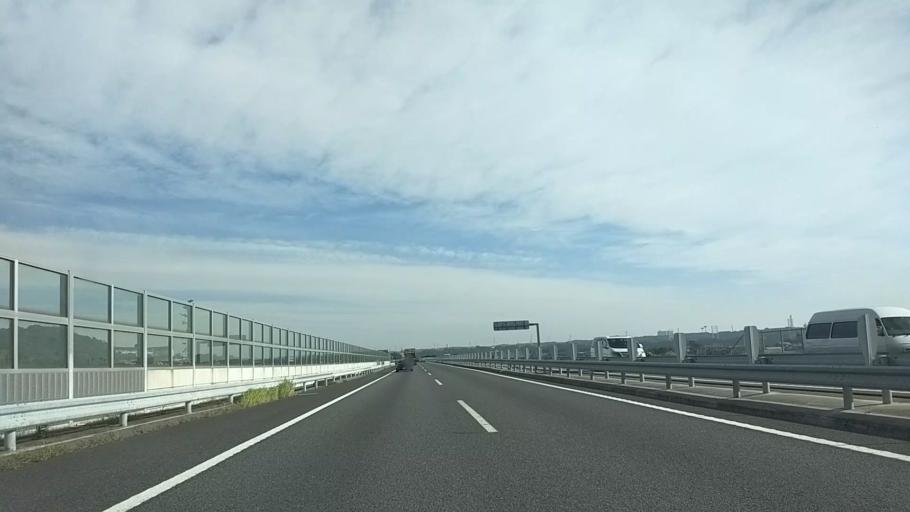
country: JP
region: Kanagawa
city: Zama
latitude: 35.5025
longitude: 139.3658
